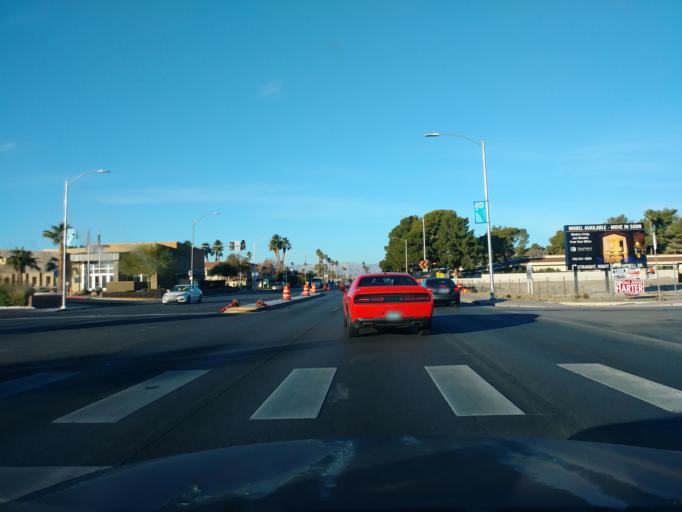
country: US
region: Nevada
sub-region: Clark County
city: Las Vegas
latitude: 36.1590
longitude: -115.1777
